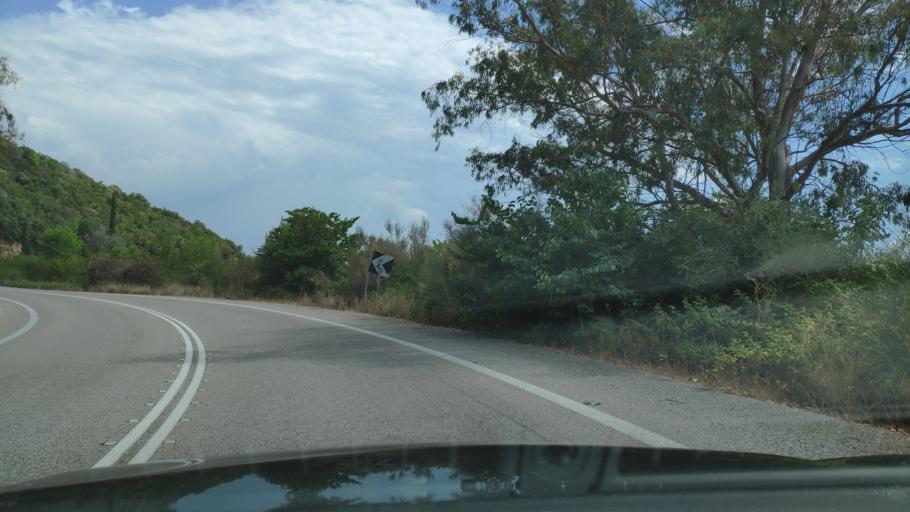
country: GR
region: West Greece
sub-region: Nomos Aitolias kai Akarnanias
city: Menidi
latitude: 39.0289
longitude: 21.1250
